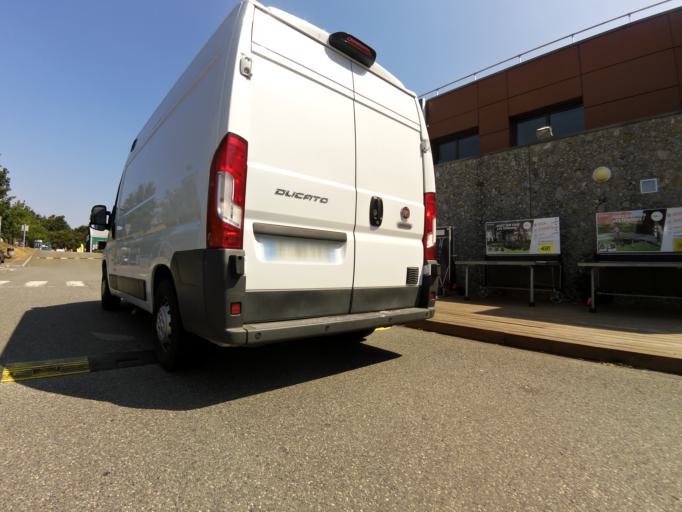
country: FR
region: Brittany
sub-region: Departement du Finistere
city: Quimper
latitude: 47.9773
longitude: -4.0793
